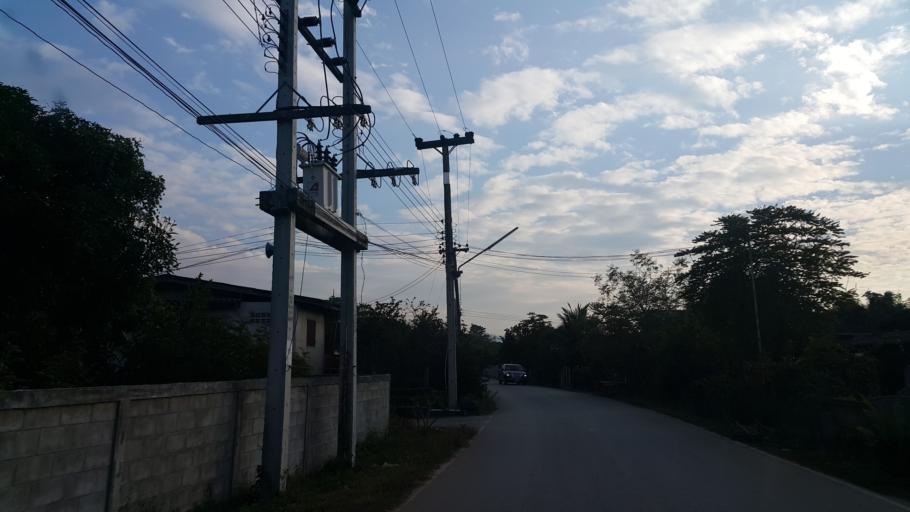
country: TH
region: Lampang
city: Sop Prap
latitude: 17.9030
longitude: 99.3289
